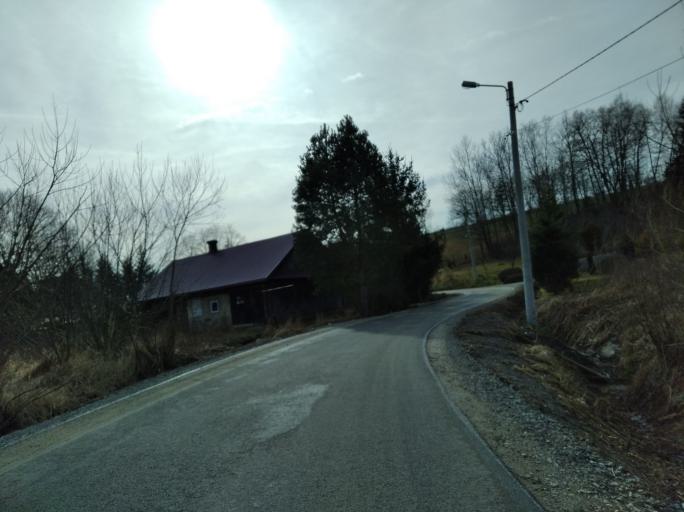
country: PL
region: Subcarpathian Voivodeship
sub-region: Powiat brzozowski
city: Jasienica Rosielna
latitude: 49.7596
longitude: 21.9479
